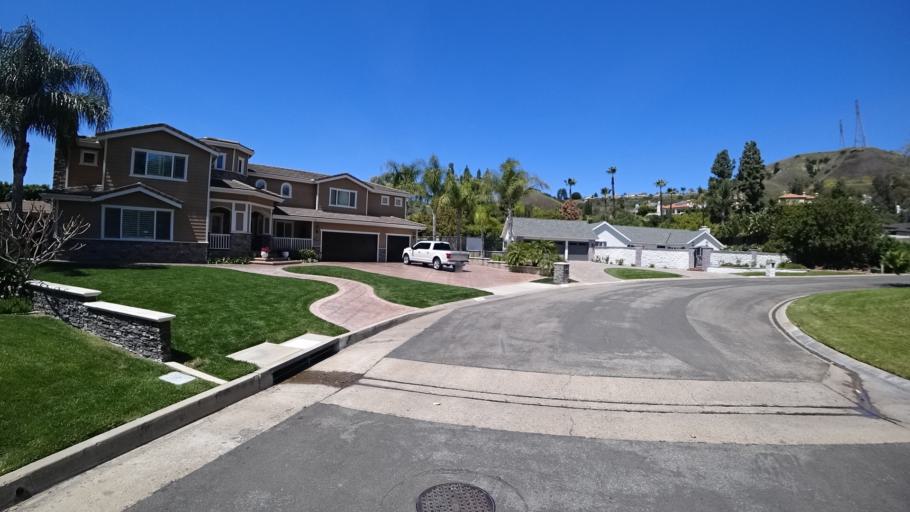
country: US
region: California
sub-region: Orange County
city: Villa Park
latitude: 33.8286
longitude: -117.8026
